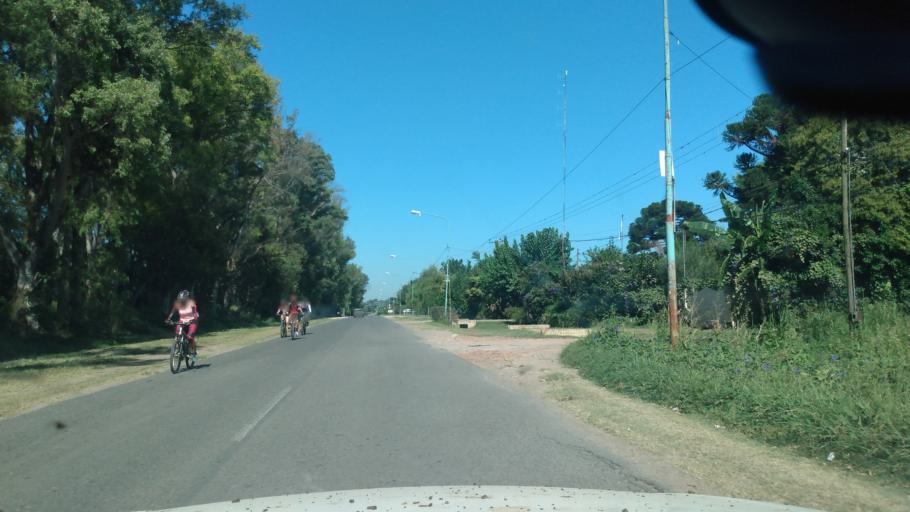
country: AR
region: Buenos Aires
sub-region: Partido de Lujan
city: Lujan
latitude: -34.5045
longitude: -59.0762
